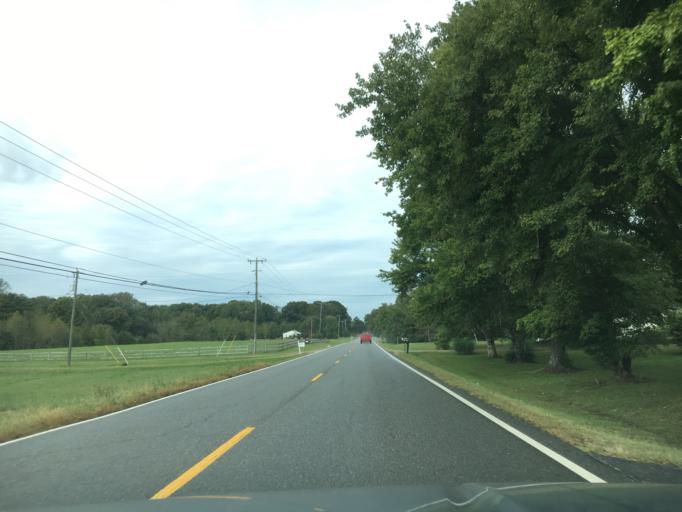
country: US
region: Virginia
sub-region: Goochland County
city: Goochland
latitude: 37.7275
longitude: -77.8332
